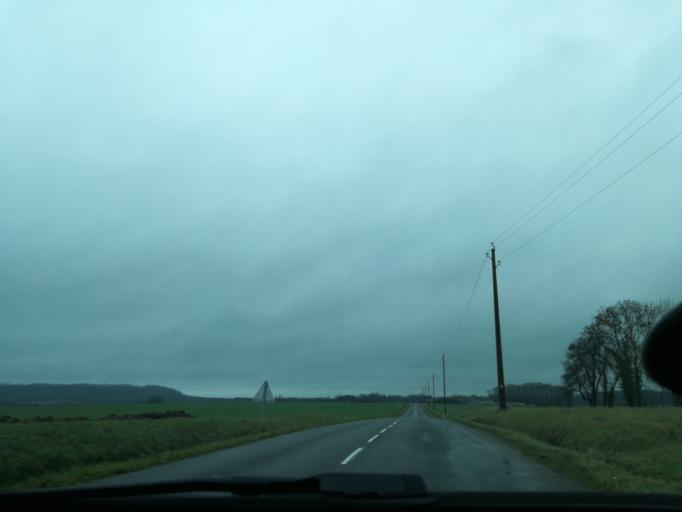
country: FR
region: Lorraine
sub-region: Departement de la Meuse
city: Clermont-en-Argonne
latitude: 49.0018
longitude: 5.0980
